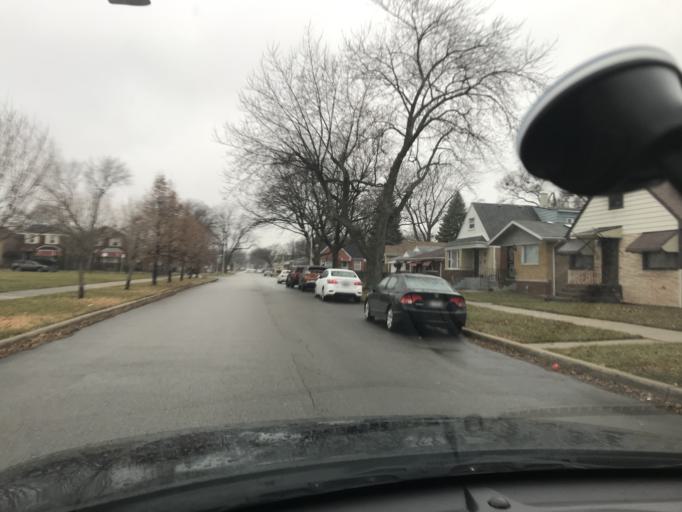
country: US
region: Illinois
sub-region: Cook County
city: Calumet Park
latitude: 41.7179
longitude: -87.6372
